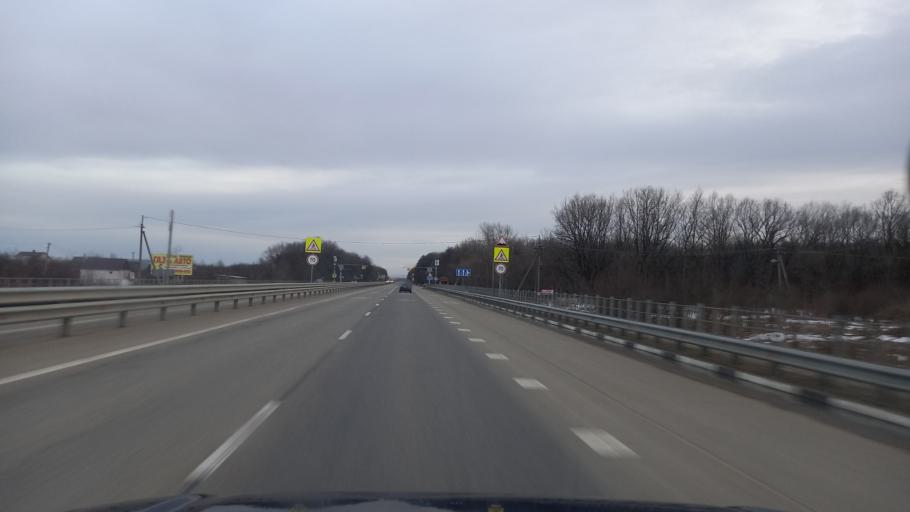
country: RU
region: Adygeya
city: Khanskaya
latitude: 44.7242
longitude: 39.9511
